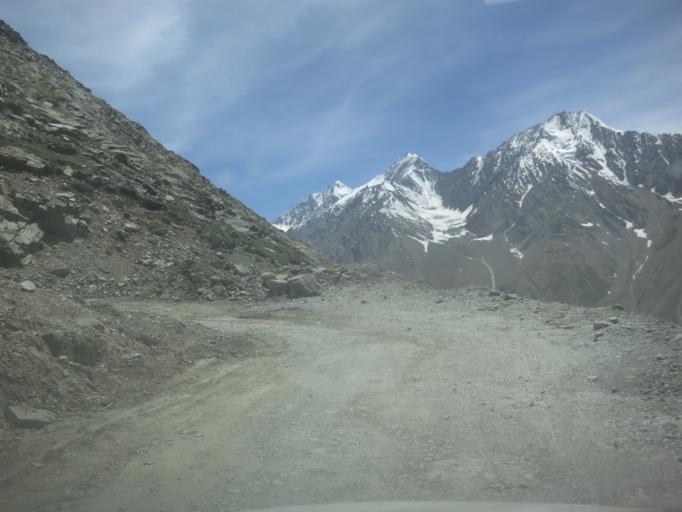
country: IN
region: Himachal Pradesh
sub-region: Kulu
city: Manali
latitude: 32.3870
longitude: 77.6262
